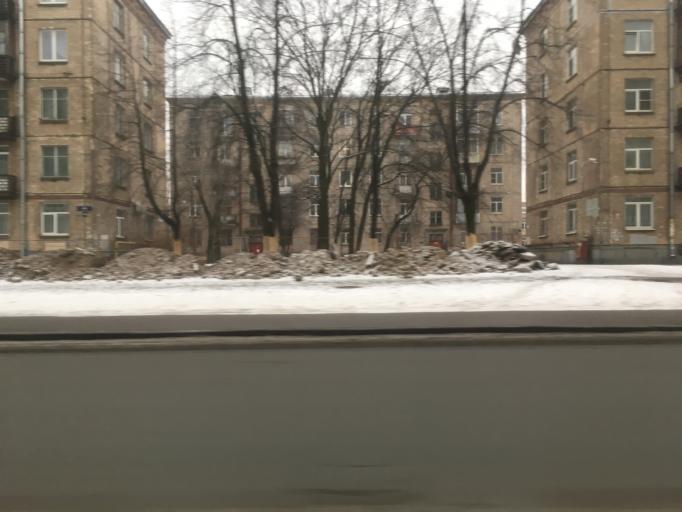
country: RU
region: St.-Petersburg
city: Obukhovo
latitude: 59.8723
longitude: 30.4384
